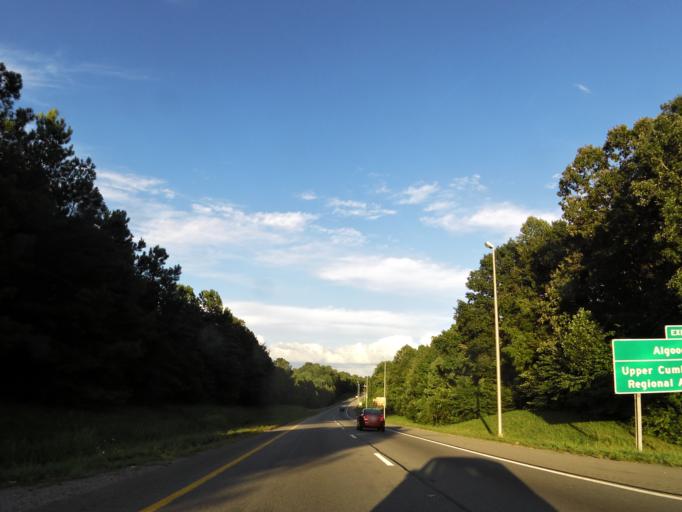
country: US
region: Tennessee
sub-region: Putnam County
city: Cookeville
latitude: 36.1371
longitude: -85.4960
